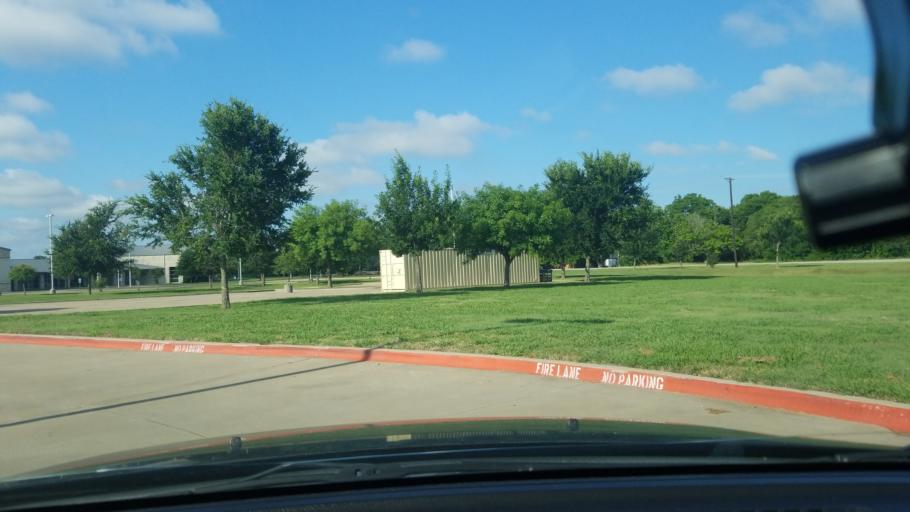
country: US
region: Texas
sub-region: Dallas County
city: Sunnyvale
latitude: 32.7979
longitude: -96.5599
